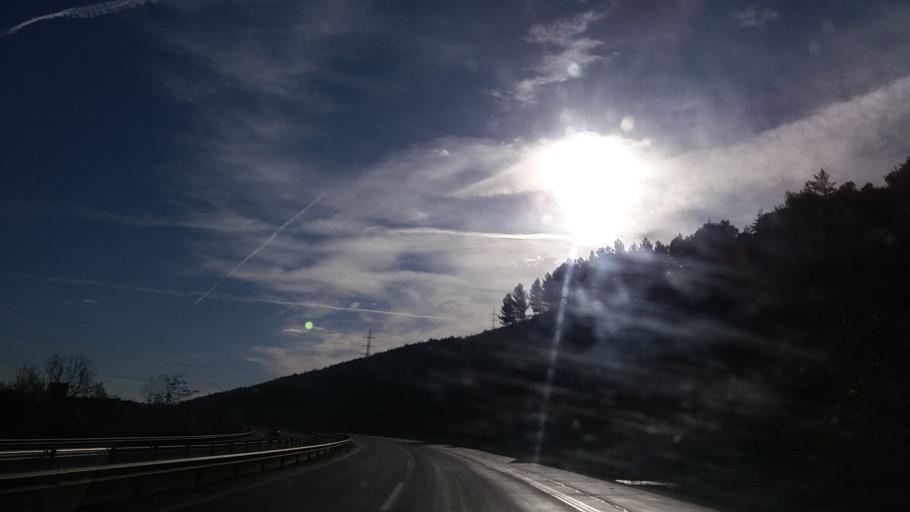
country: ES
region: Navarre
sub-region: Provincia de Navarra
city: Orkoien
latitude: 42.8032
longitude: -1.7125
